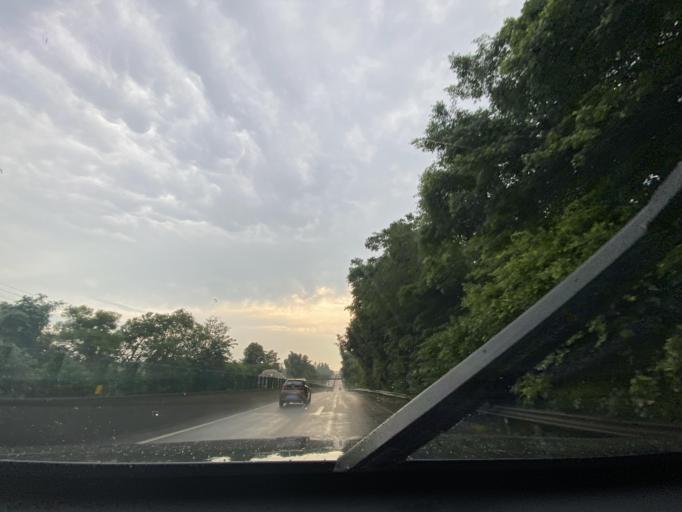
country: CN
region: Sichuan
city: Chonglong
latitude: 29.7655
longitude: 104.7839
